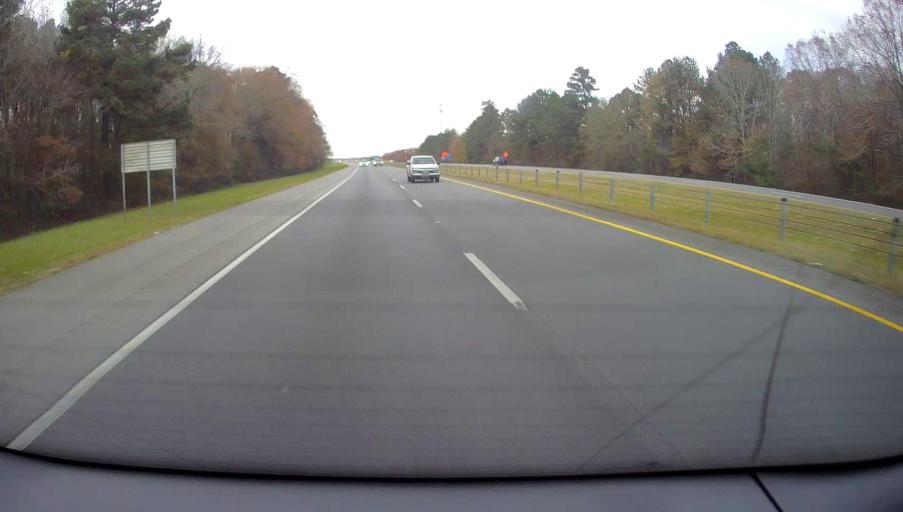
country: US
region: Alabama
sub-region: Limestone County
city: Athens
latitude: 34.7114
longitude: -86.9301
